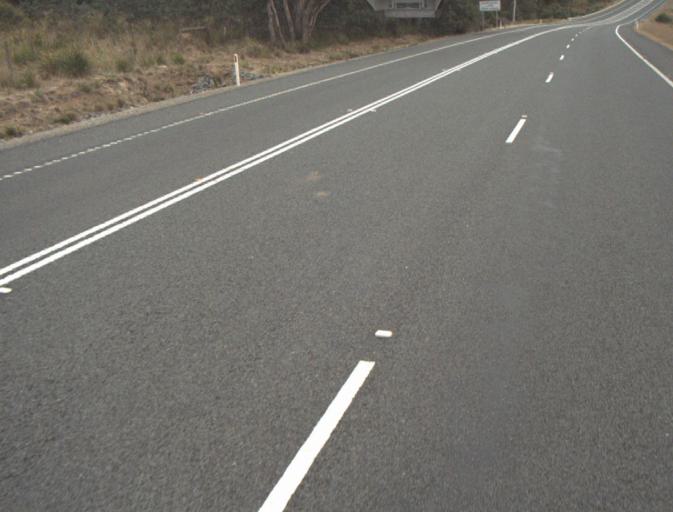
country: AU
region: Tasmania
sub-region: Launceston
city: Mayfield
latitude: -41.2632
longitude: 147.0302
